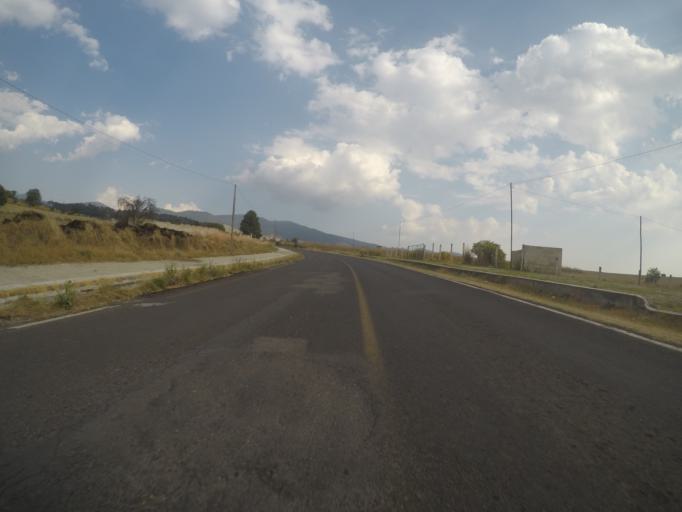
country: MX
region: Mexico
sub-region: Xalatlaco
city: El Aguila (La Mesa)
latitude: 19.1597
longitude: -99.4043
